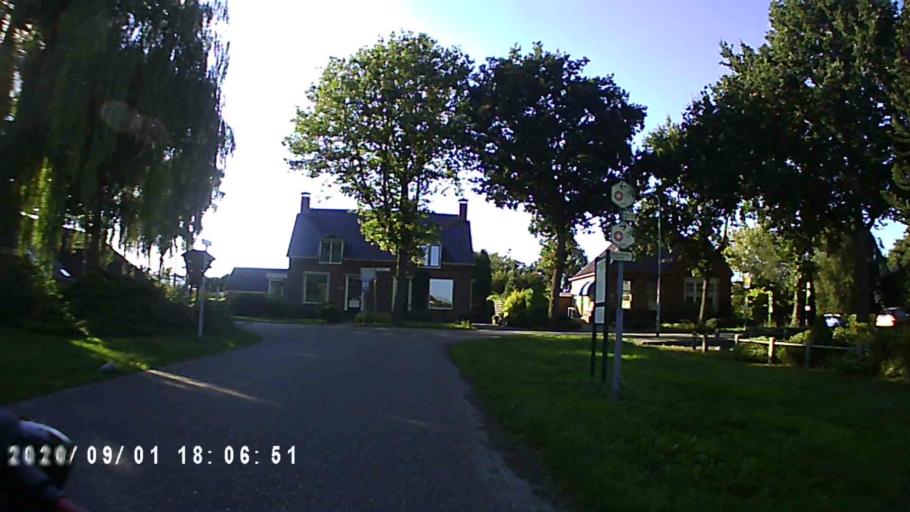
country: NL
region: Groningen
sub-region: Gemeente Slochteren
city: Slochteren
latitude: 53.2007
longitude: 6.7897
